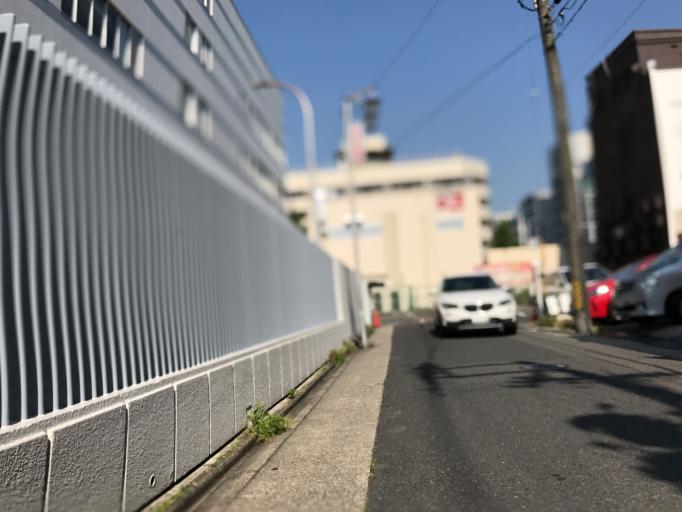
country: JP
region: Aichi
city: Nagoya-shi
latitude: 35.1694
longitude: 136.9380
